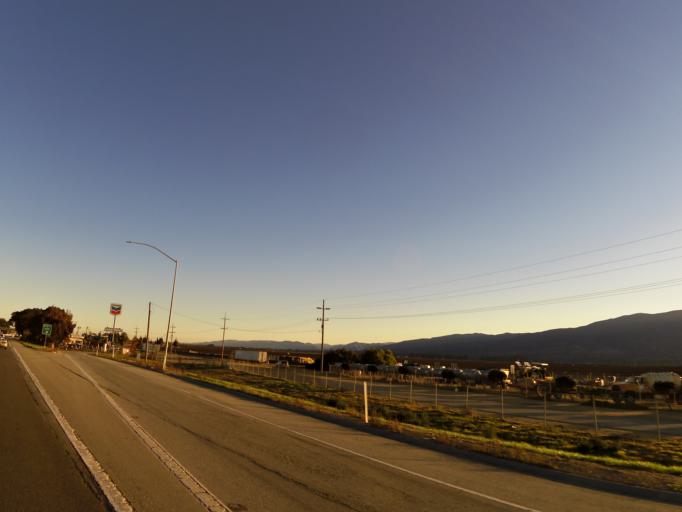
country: US
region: California
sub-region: Monterey County
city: Soledad
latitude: 36.4517
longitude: -121.3671
